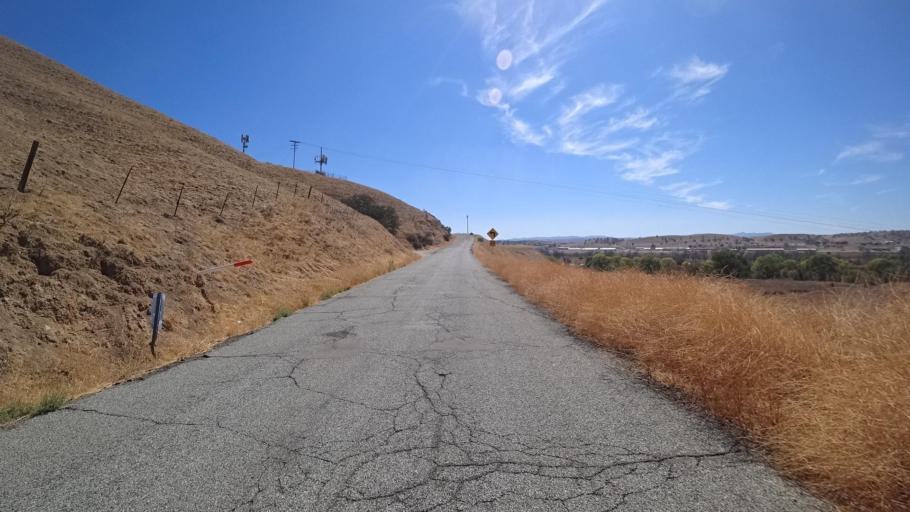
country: US
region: California
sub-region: San Luis Obispo County
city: San Miguel
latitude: 35.7919
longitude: -120.7184
